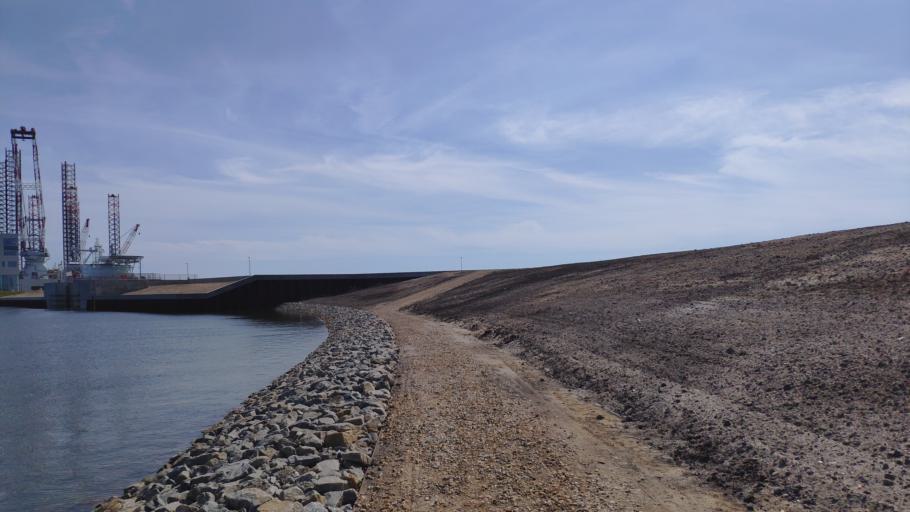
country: DK
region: South Denmark
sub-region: Fano Kommune
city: Nordby
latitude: 55.4827
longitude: 8.4080
